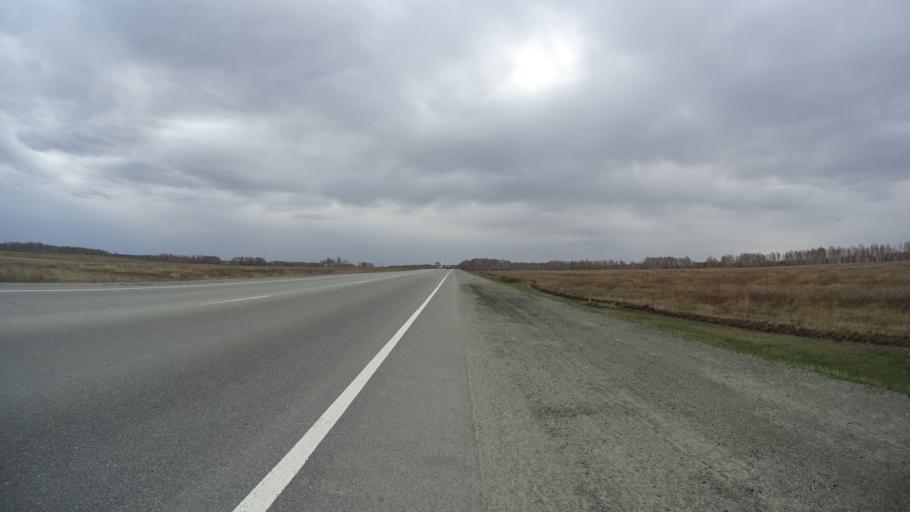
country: RU
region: Chelyabinsk
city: Yemanzhelinsk
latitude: 54.7043
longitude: 61.2553
